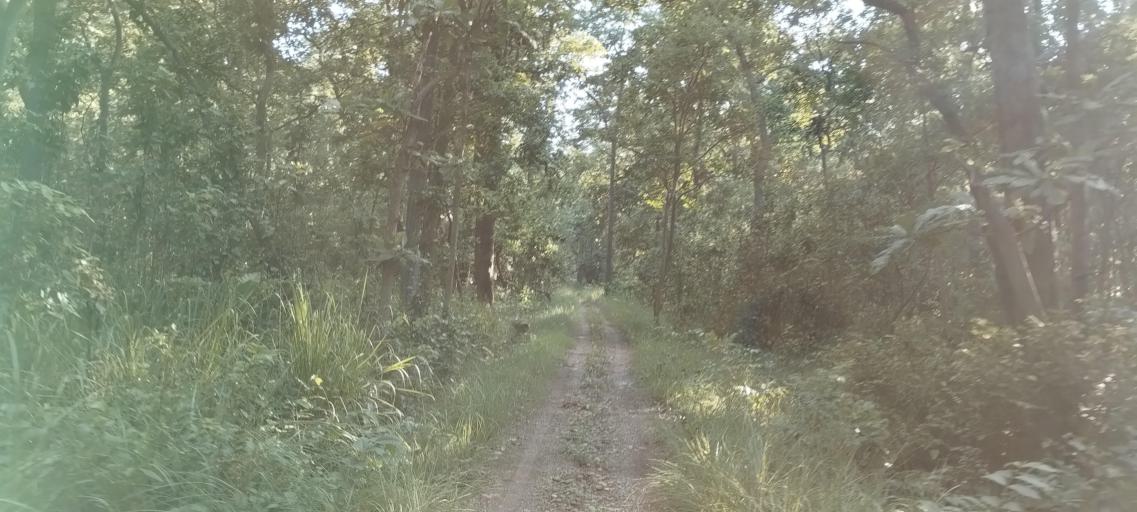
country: NP
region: Far Western
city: Tikapur
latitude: 28.5137
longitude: 81.2718
